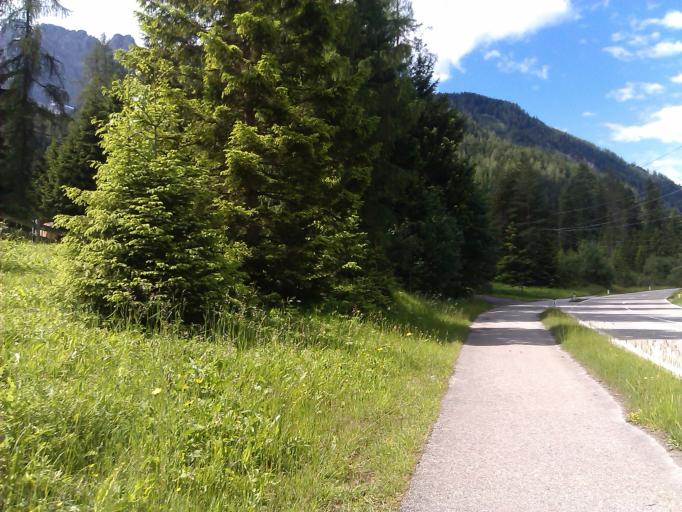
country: AT
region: Tyrol
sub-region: Politischer Bezirk Reutte
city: Biberwier
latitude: 47.3670
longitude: 10.8808
